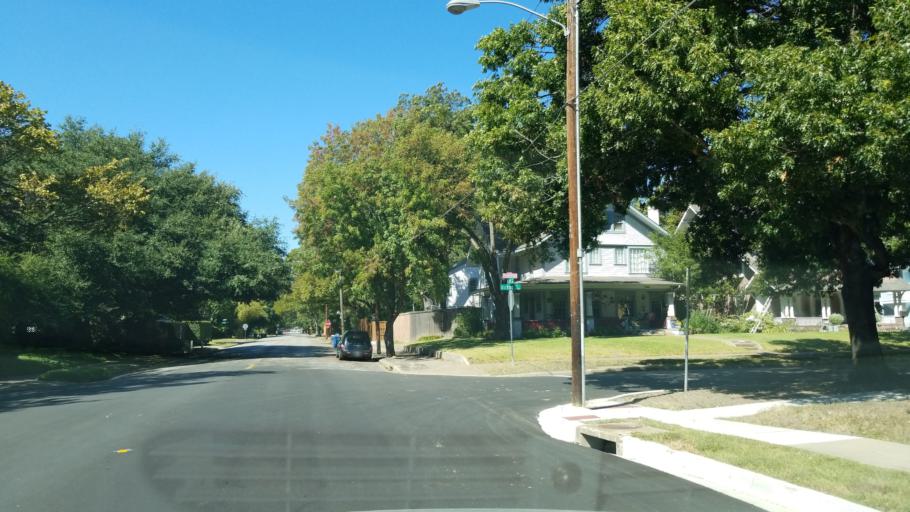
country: US
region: Texas
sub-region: Dallas County
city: Highland Park
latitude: 32.7984
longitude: -96.7640
